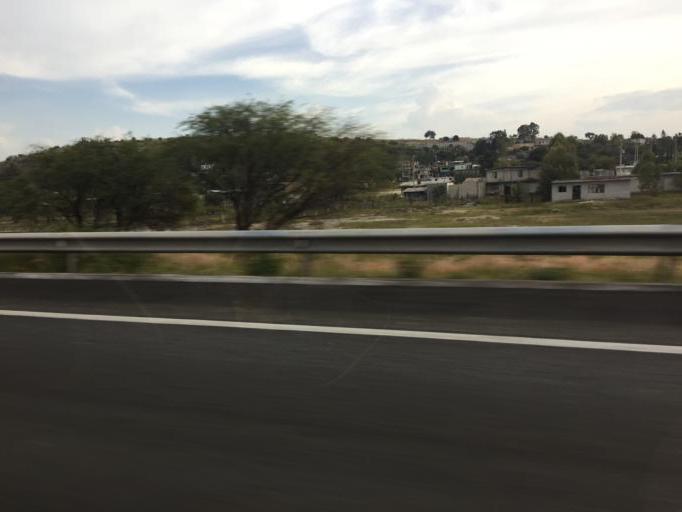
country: MX
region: Michoacan
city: Querendaro
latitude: 19.8856
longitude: -100.9482
